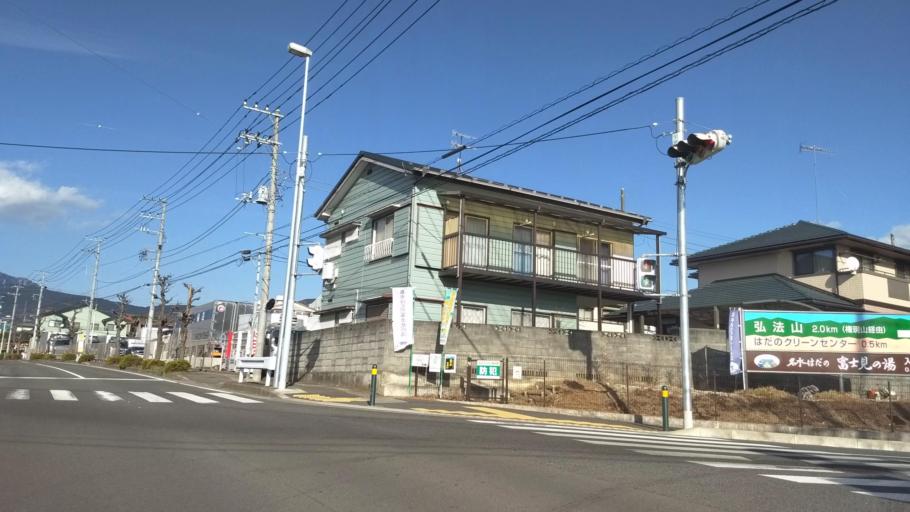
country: JP
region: Kanagawa
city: Hadano
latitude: 35.3743
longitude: 139.2352
